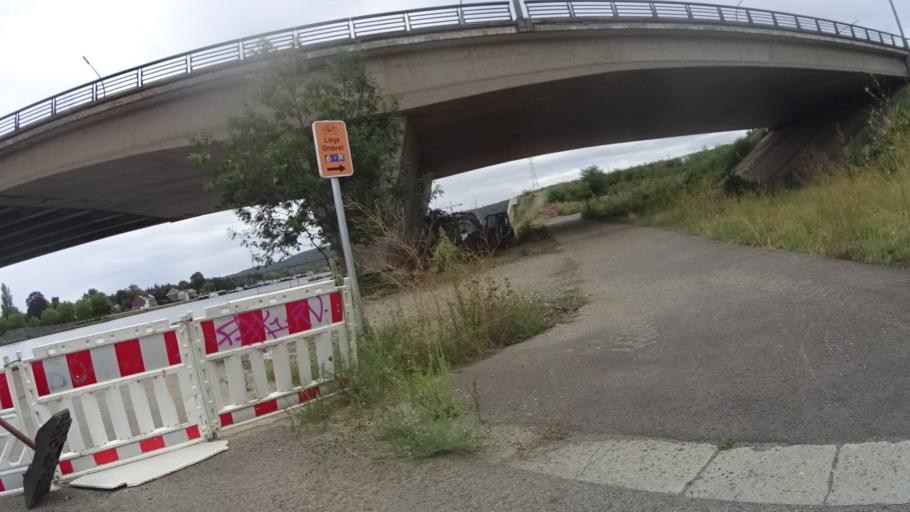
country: BE
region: Wallonia
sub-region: Province de Liege
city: Amay
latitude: 50.5350
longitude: 5.2826
